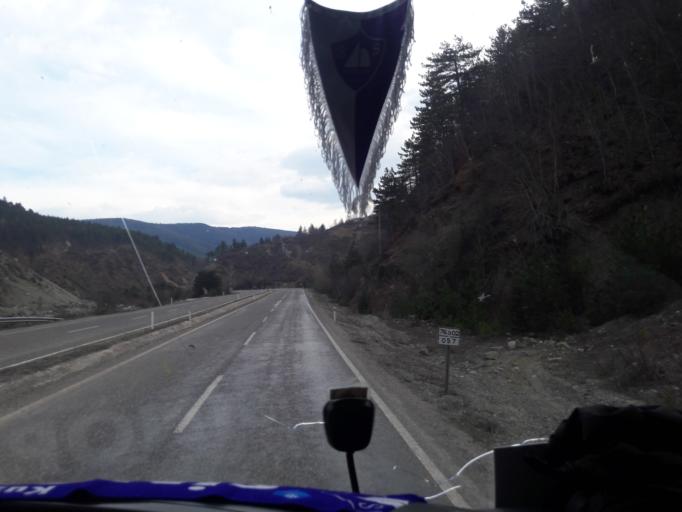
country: TR
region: Kastamonu
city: Kuzyaka
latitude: 41.1840
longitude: 33.7973
